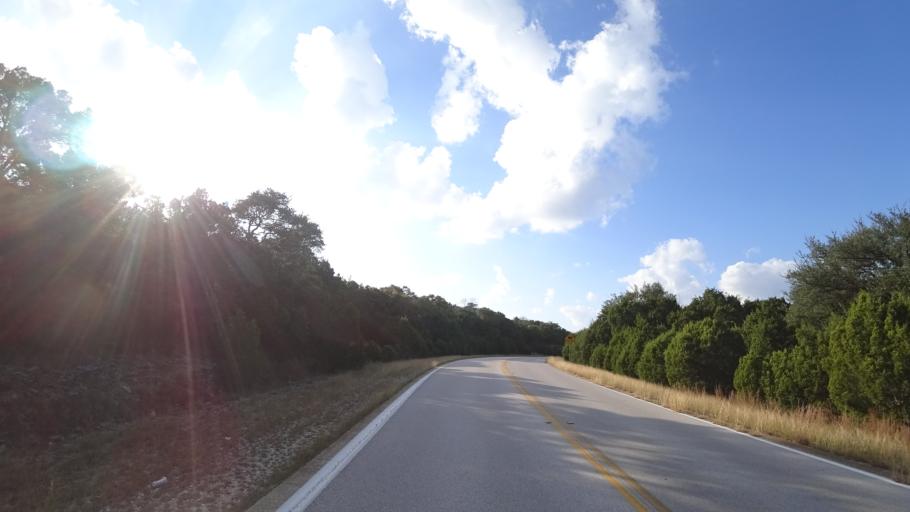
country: US
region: Texas
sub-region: Travis County
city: Barton Creek
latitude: 30.2699
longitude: -97.8514
